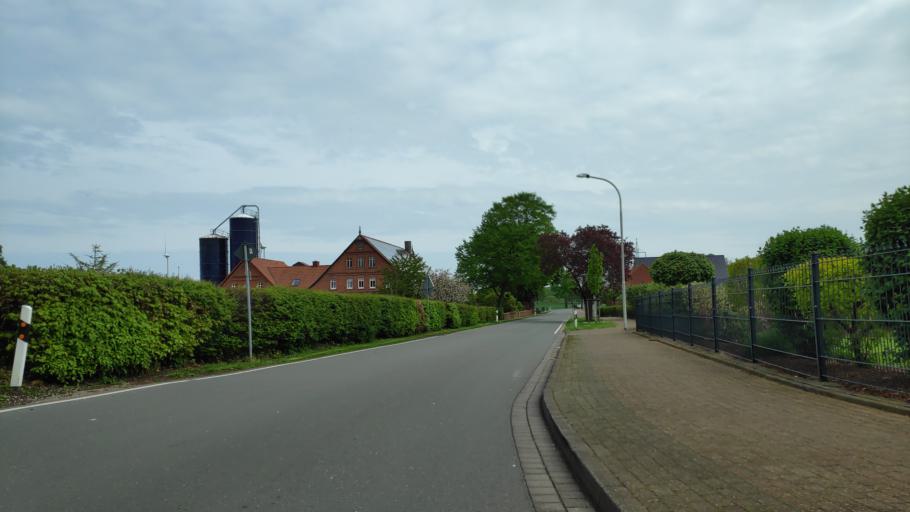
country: DE
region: North Rhine-Westphalia
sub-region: Regierungsbezirk Detmold
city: Petershagen
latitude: 52.3202
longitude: 8.9898
